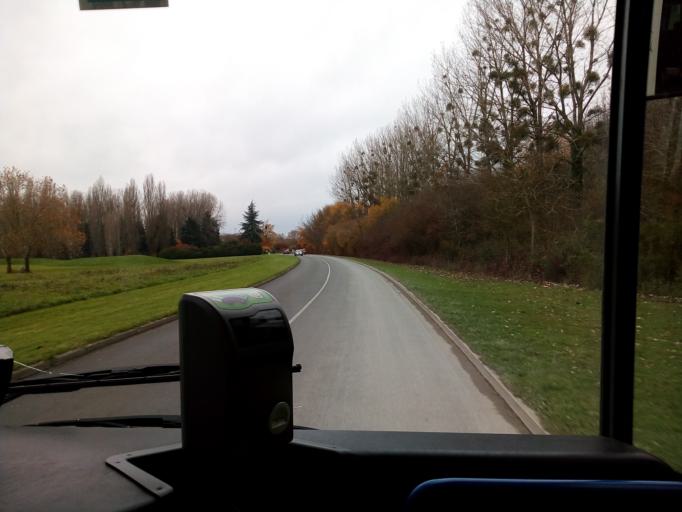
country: FR
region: Ile-de-France
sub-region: Departement de l'Essonne
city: Villebon-sur-Yvette
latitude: 48.7151
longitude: 2.2204
